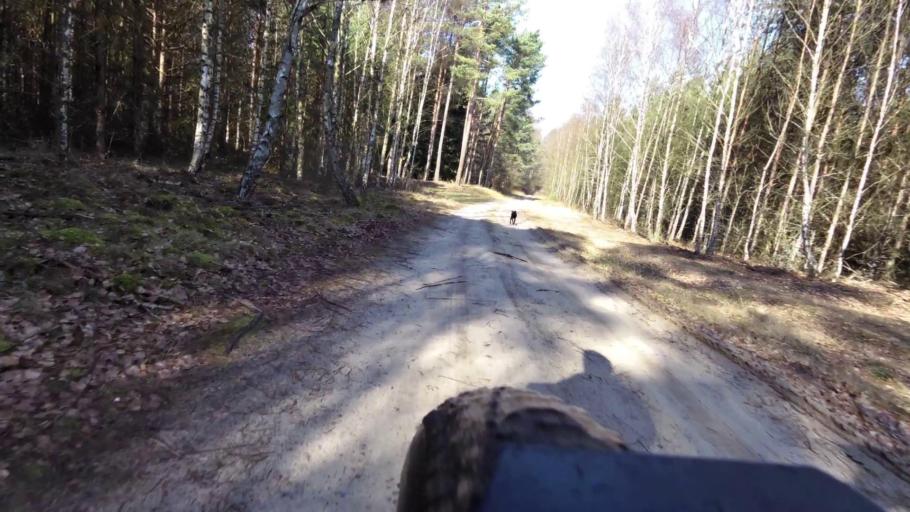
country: PL
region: Lubusz
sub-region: Powiat sulecinski
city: Torzym
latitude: 52.2216
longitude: 14.9768
